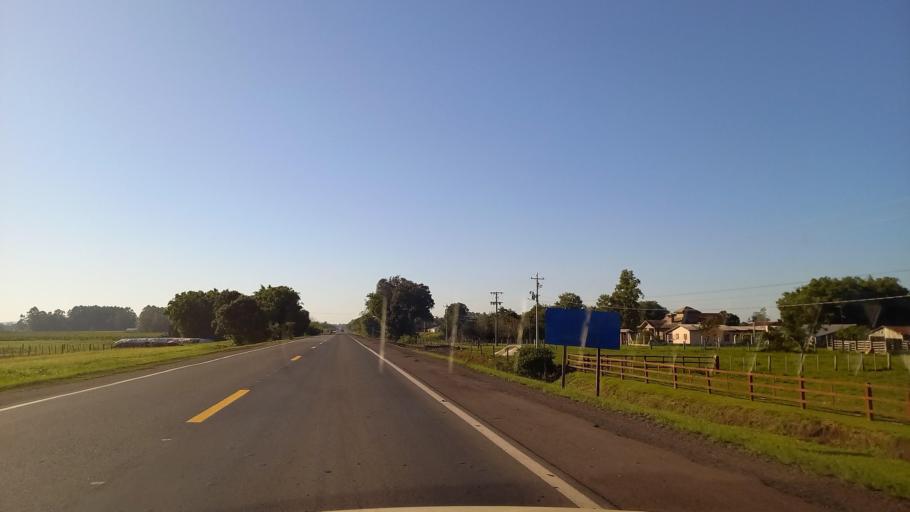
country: BR
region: Rio Grande do Sul
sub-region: Venancio Aires
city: Venancio Aires
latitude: -29.6618
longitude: -52.0663
